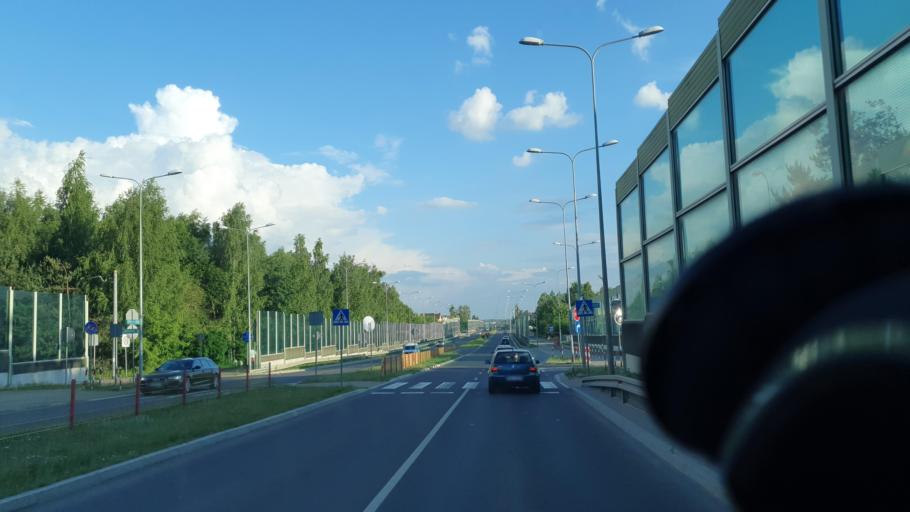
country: PL
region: Podlasie
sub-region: Powiat bialostocki
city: Wasilkow
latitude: 53.1556
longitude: 23.2025
